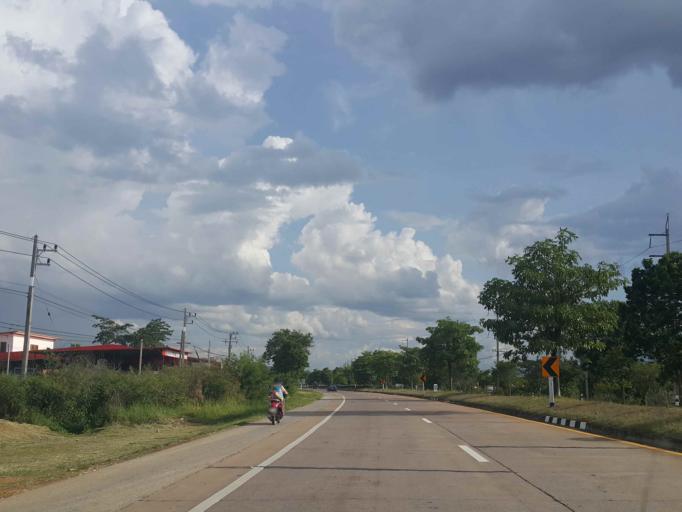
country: TH
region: Phrae
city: Sung Men
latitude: 18.0124
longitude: 100.1061
